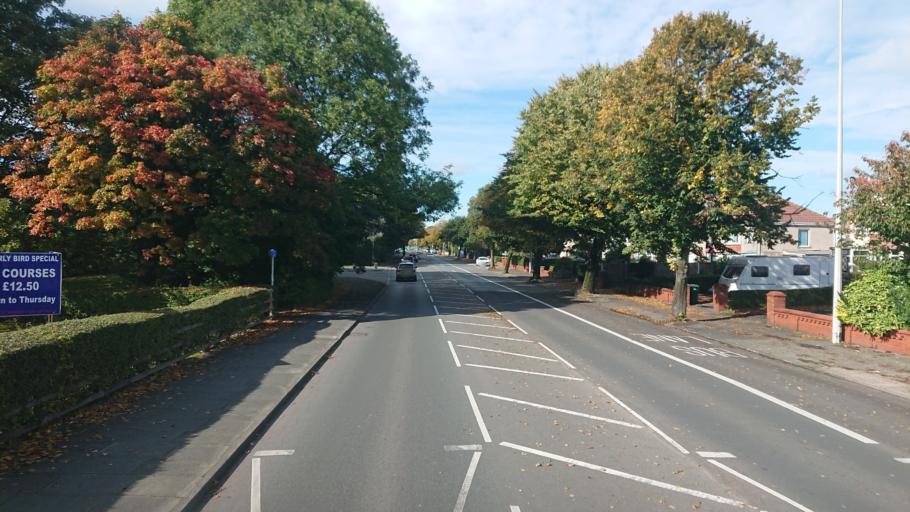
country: GB
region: England
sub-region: Lancashire
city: Lancaster
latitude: 54.0576
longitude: -2.8205
